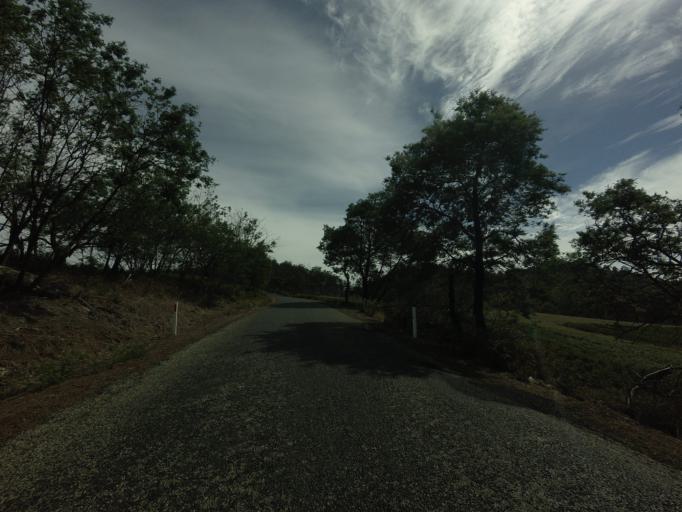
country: AU
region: Tasmania
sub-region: Sorell
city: Sorell
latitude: -42.5721
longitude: 147.6937
